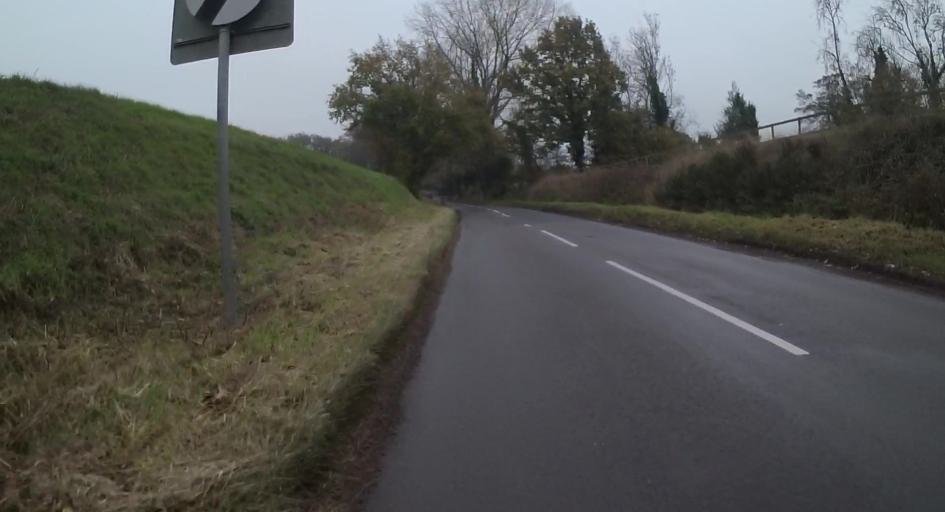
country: GB
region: England
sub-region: Hampshire
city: Kingsley
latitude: 51.1645
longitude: -0.8822
